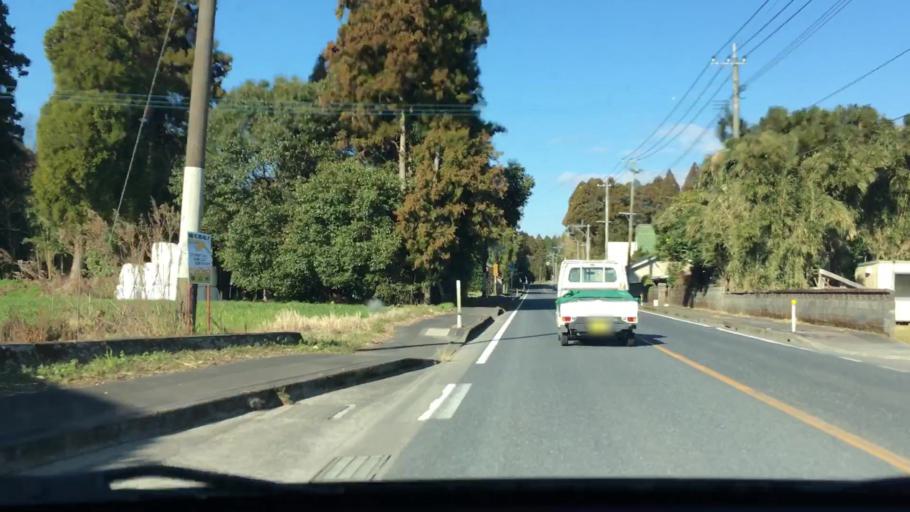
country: JP
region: Kagoshima
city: Kokubu-matsuki
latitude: 31.6710
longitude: 130.8647
